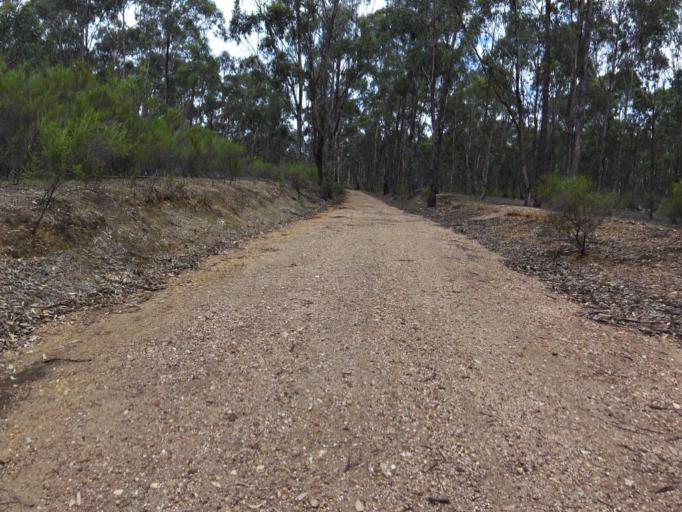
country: AU
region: Victoria
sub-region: Greater Bendigo
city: Kennington
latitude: -36.8884
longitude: 144.6602
